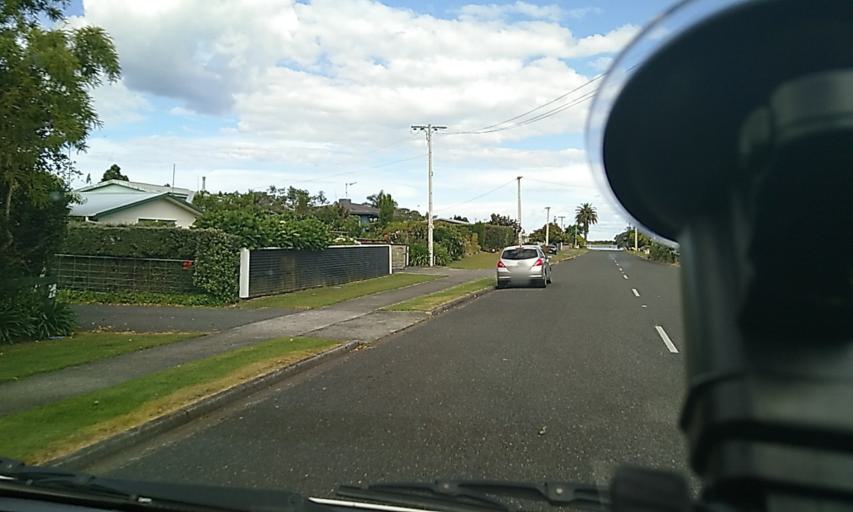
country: NZ
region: Bay of Plenty
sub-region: Western Bay of Plenty District
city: Waihi Beach
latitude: -37.4463
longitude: 175.9645
